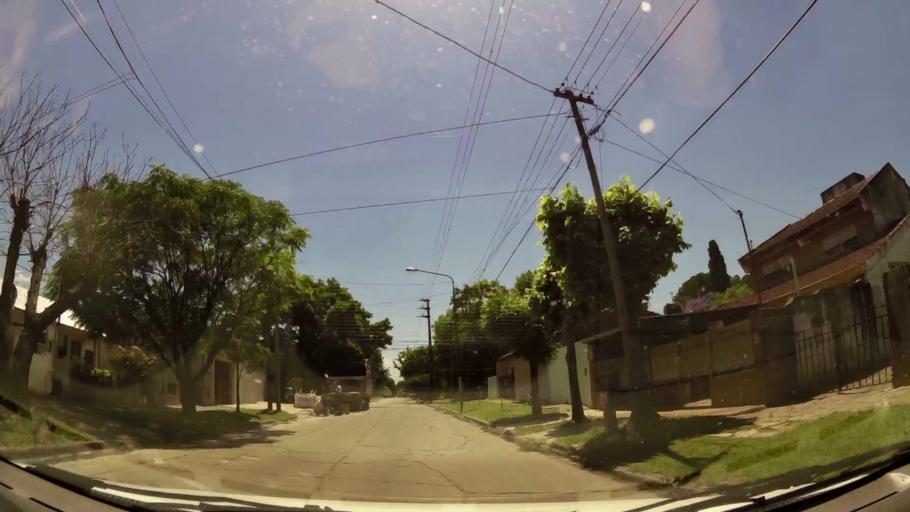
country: AR
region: Buenos Aires
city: Ituzaingo
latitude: -34.6619
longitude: -58.6824
